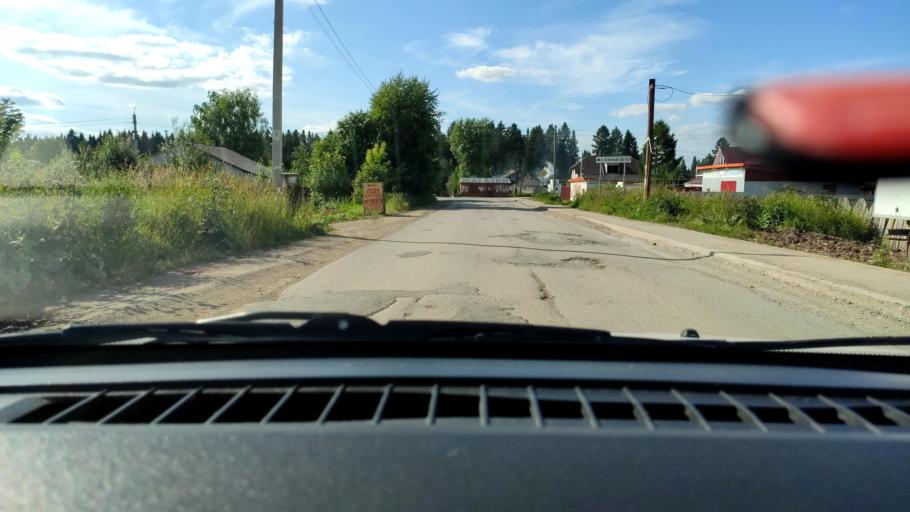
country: RU
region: Perm
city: Kultayevo
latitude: 57.8997
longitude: 55.9604
